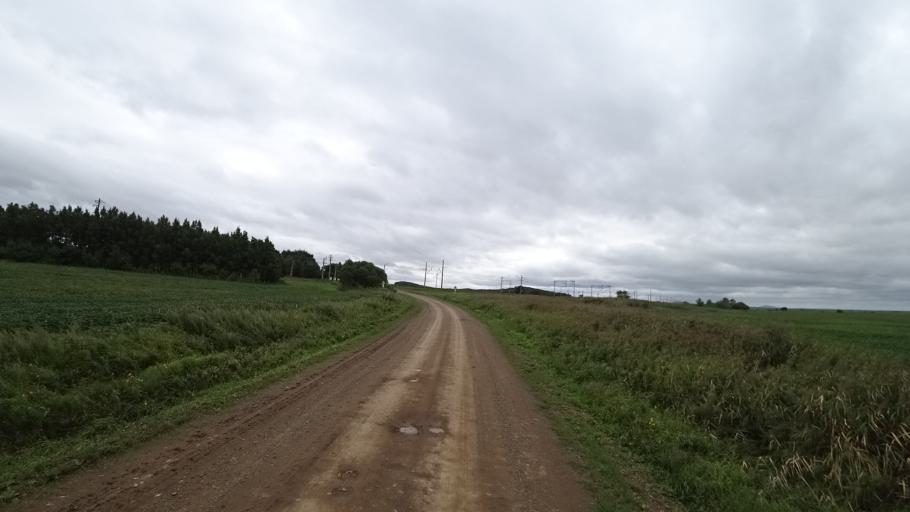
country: RU
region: Primorskiy
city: Chernigovka
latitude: 44.4811
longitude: 132.5748
